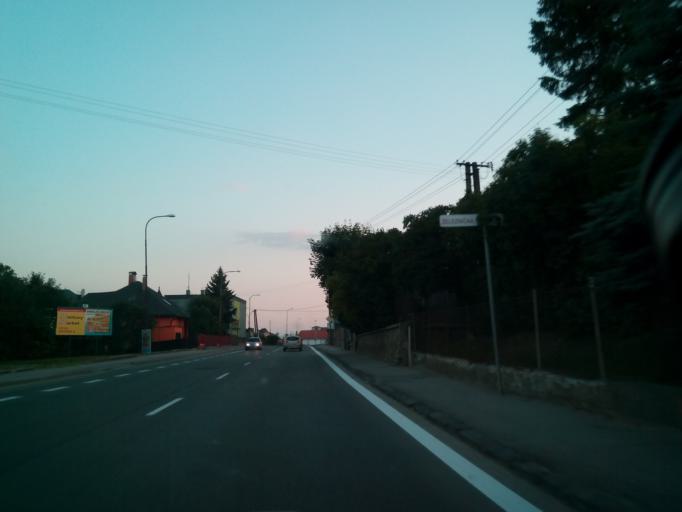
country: SK
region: Presovsky
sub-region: Okres Presov
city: Kezmarok
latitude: 49.1407
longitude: 20.4263
